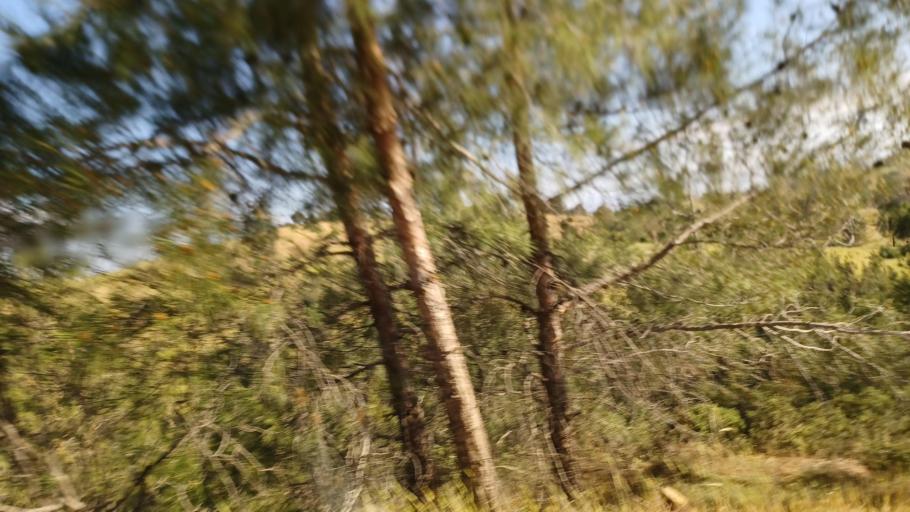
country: CY
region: Lefkosia
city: Peristerona
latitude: 35.0295
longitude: 33.0564
